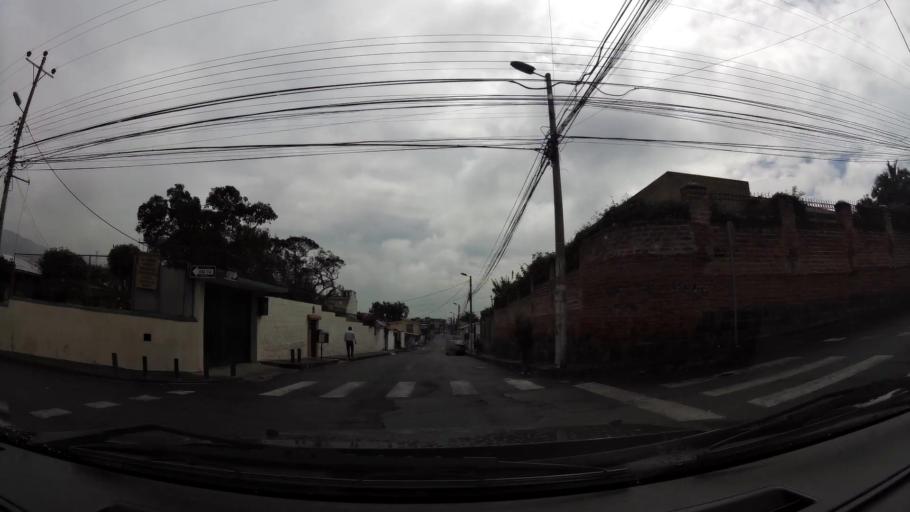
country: EC
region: Pichincha
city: Sangolqui
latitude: -0.2958
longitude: -78.4775
